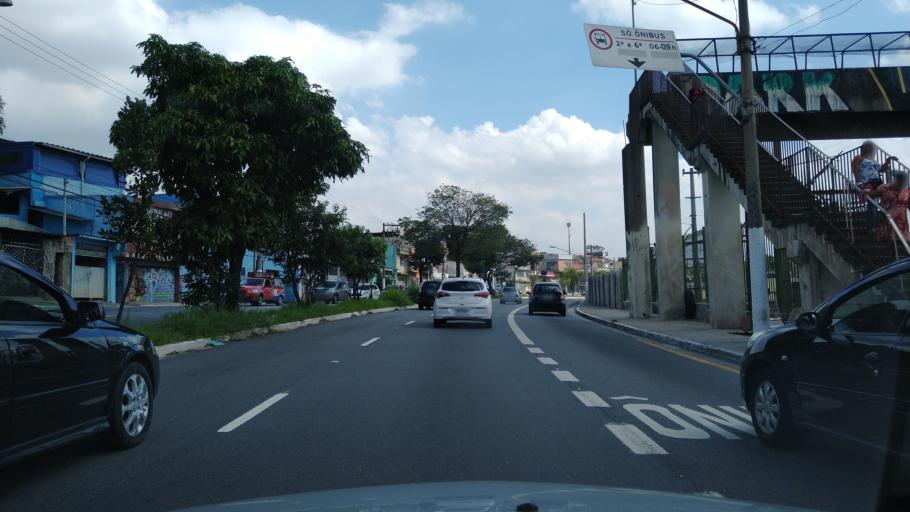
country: BR
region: Sao Paulo
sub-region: Guarulhos
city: Guarulhos
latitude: -23.5086
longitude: -46.5434
